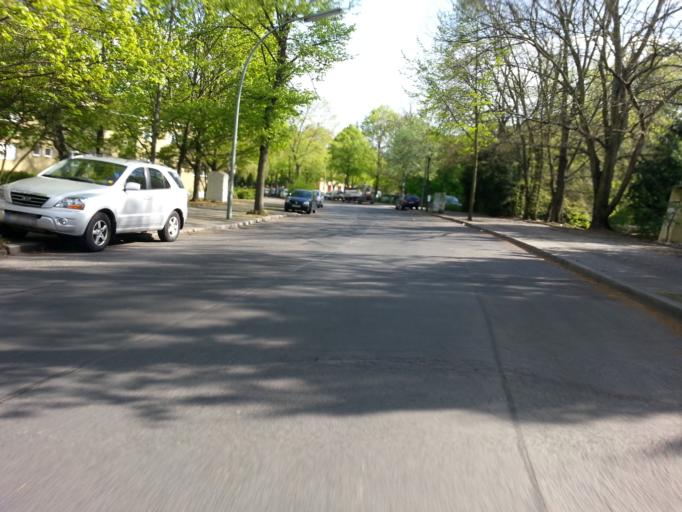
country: DE
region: Berlin
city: Charlottenburg-Nord
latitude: 52.5367
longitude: 13.2797
